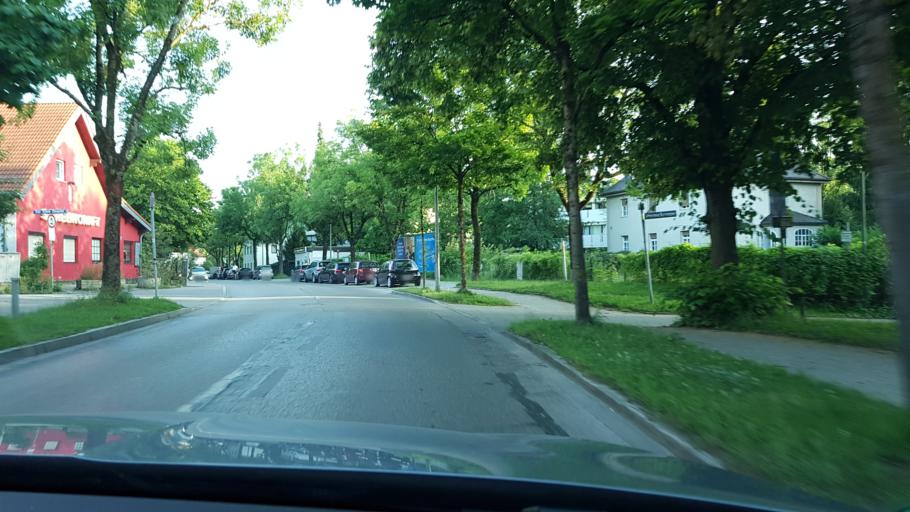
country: DE
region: Bavaria
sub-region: Upper Bavaria
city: Bogenhausen
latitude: 48.1696
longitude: 11.6242
